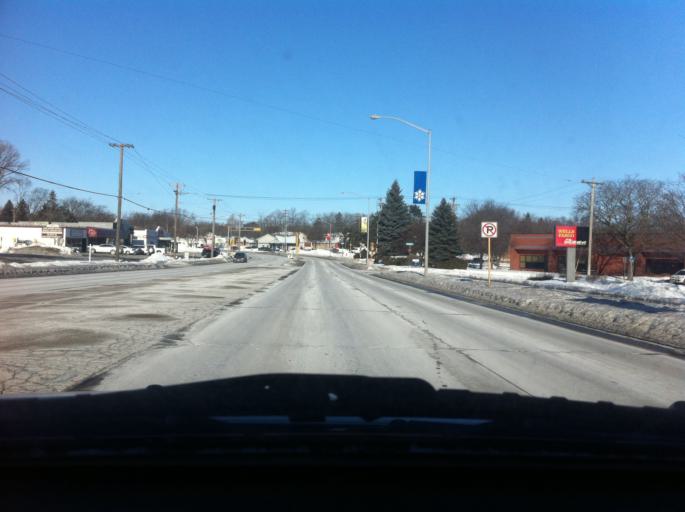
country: US
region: Wisconsin
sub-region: Dane County
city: Middleton
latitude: 43.0954
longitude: -89.4941
